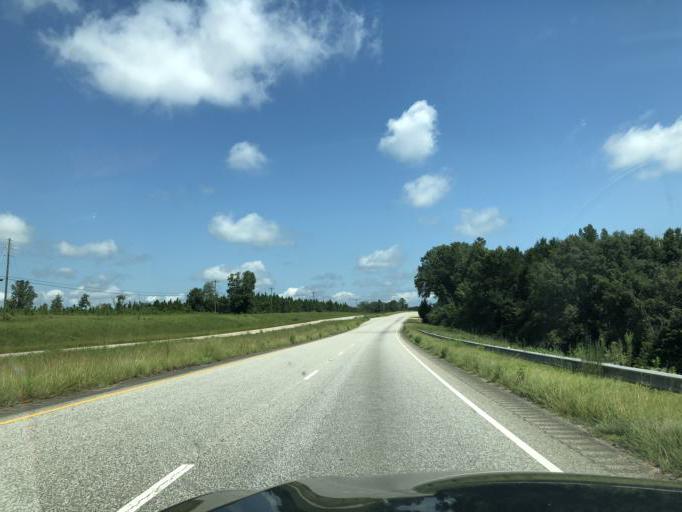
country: US
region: Alabama
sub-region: Henry County
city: Abbeville
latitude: 31.7138
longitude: -85.2725
